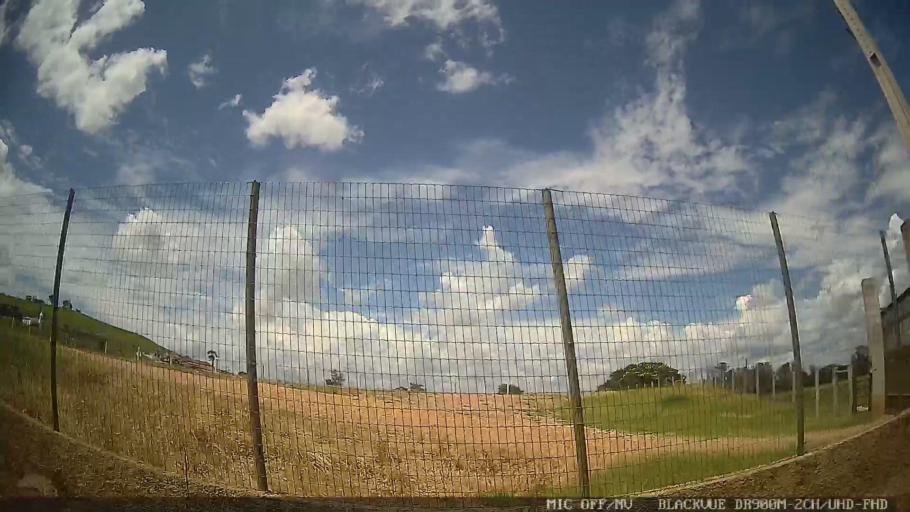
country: BR
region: Sao Paulo
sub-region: Conchas
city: Conchas
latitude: -23.0538
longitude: -47.9846
